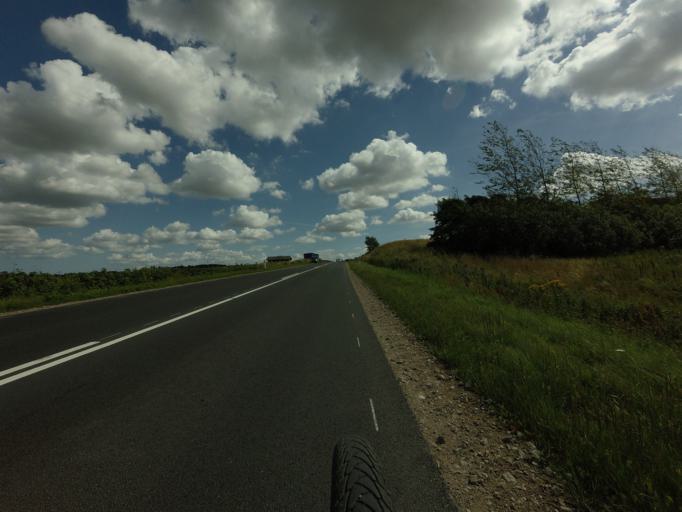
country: DK
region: North Denmark
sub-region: Hjorring Kommune
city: Hjorring
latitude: 57.4529
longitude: 9.9125
